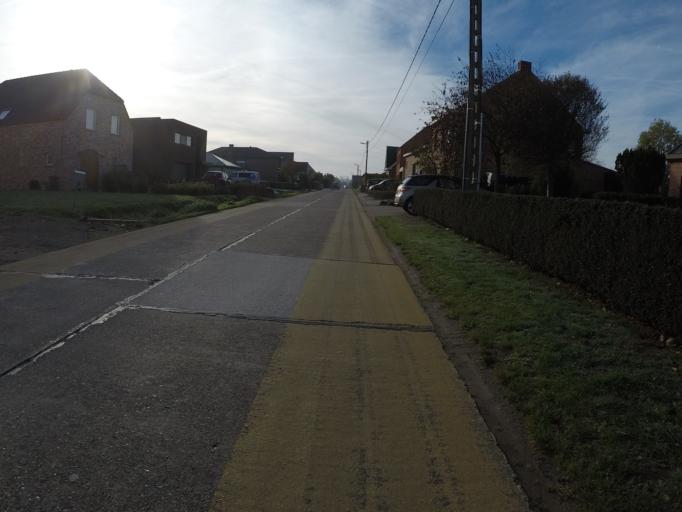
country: BE
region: Flanders
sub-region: Provincie Vlaams-Brabant
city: Begijnendijk
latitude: 50.9897
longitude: 4.7751
